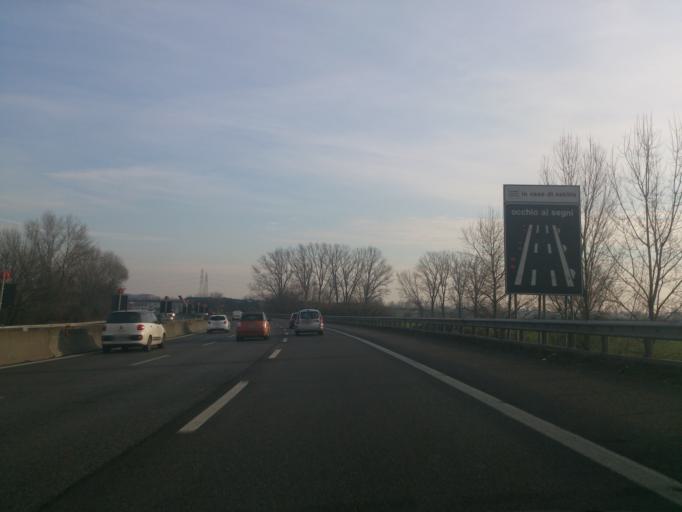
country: IT
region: Lombardy
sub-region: Citta metropolitana di Milano
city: Chiaravalle
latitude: 45.4186
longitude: 9.2467
